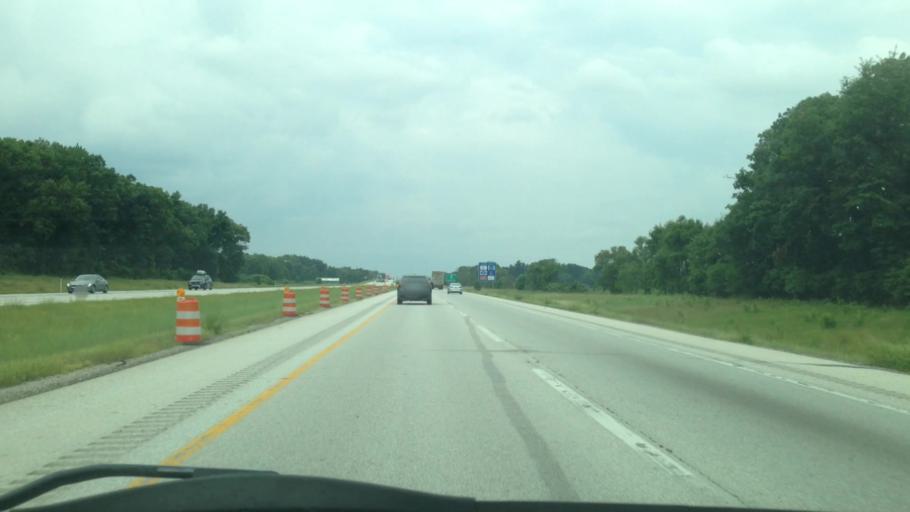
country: US
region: Indiana
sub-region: Elkhart County
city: Simonton Lake
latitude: 41.7303
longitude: -85.9362
